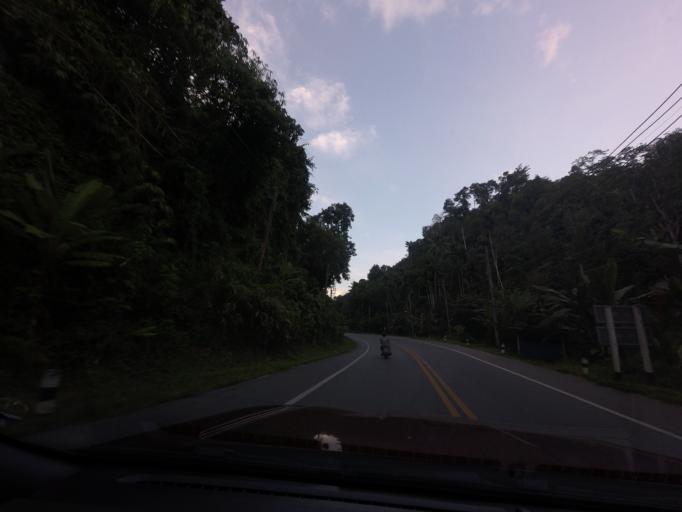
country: TH
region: Yala
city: Than To
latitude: 6.0647
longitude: 101.1957
